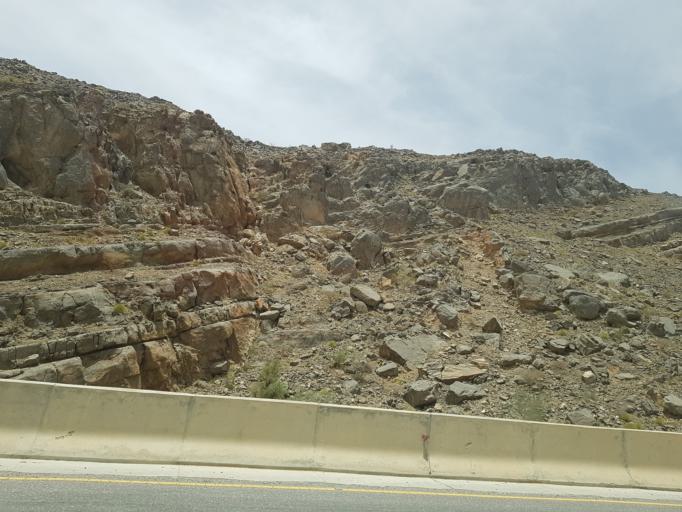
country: OM
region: Muhafazat ad Dakhiliyah
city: Izki
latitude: 22.9565
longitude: 57.6748
